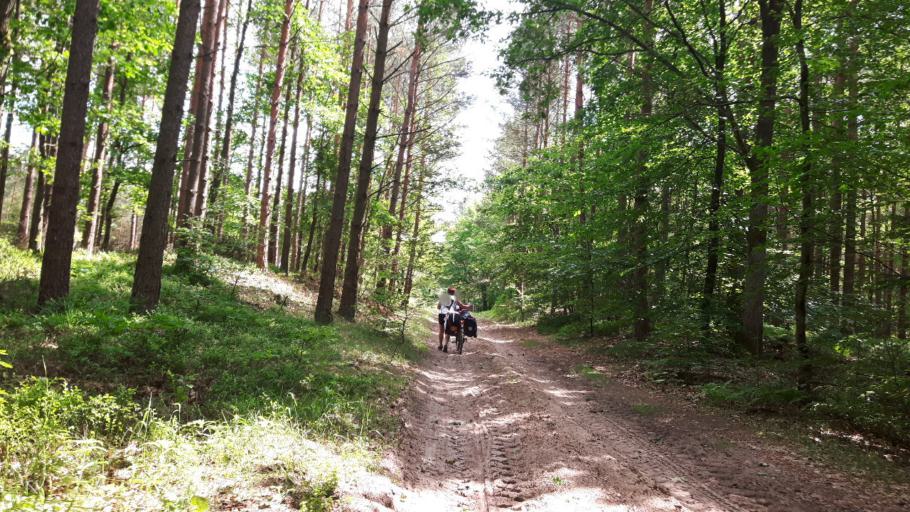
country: PL
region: West Pomeranian Voivodeship
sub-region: Powiat goleniowski
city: Osina
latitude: 53.6528
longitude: 14.9097
